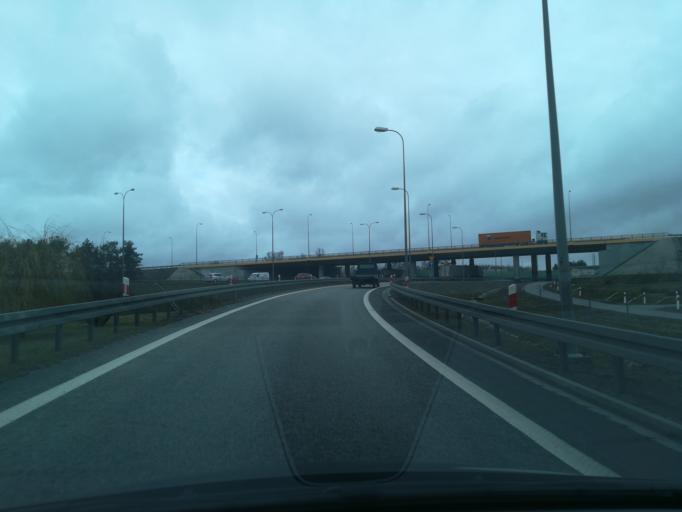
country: PL
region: Kujawsko-Pomorskie
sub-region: Powiat torunski
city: Lubicz Dolny
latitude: 53.0371
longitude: 18.7336
